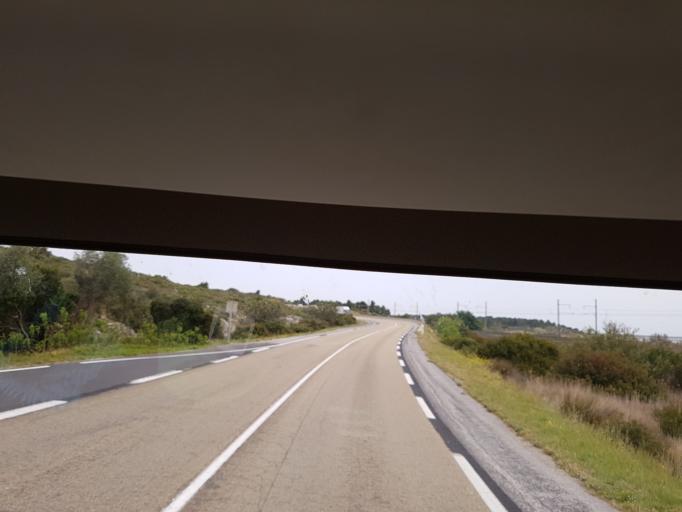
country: FR
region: Languedoc-Roussillon
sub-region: Departement de l'Aude
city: Leucate
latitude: 42.8716
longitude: 2.9891
